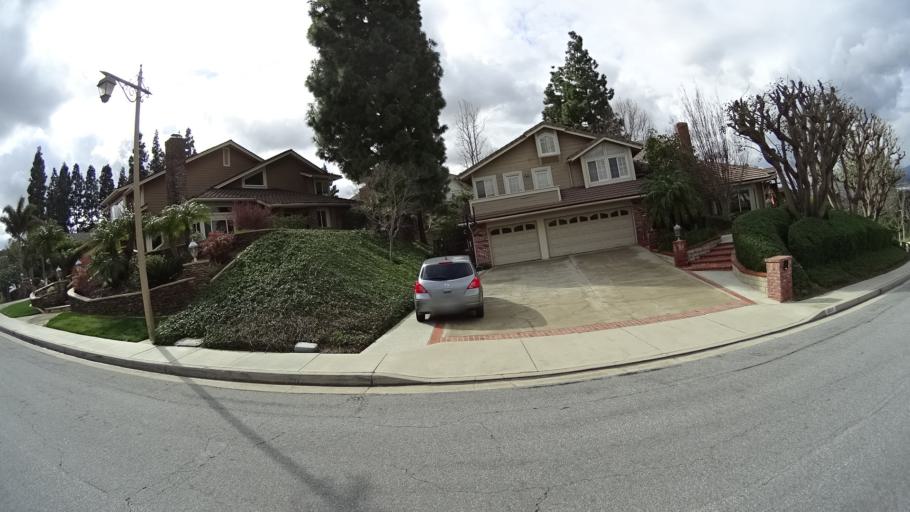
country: US
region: California
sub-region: Orange County
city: Villa Park
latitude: 33.8411
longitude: -117.7872
